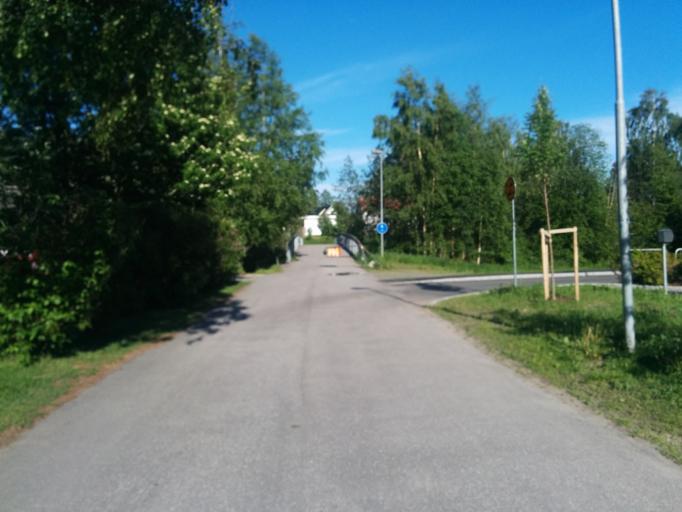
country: SE
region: Vaesterbotten
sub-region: Umea Kommun
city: Hoernefors
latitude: 63.6297
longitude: 19.9098
